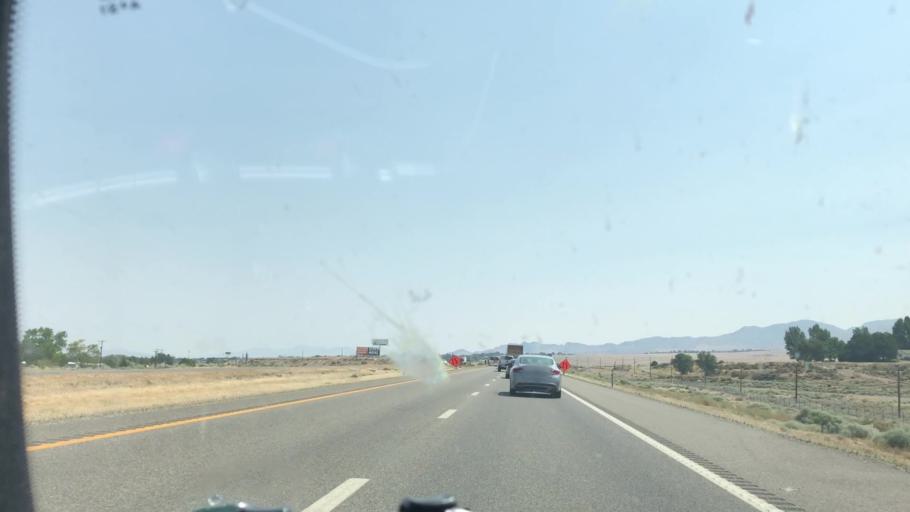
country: US
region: Nevada
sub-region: Humboldt County
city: Winnemucca
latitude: 40.9438
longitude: -117.7707
